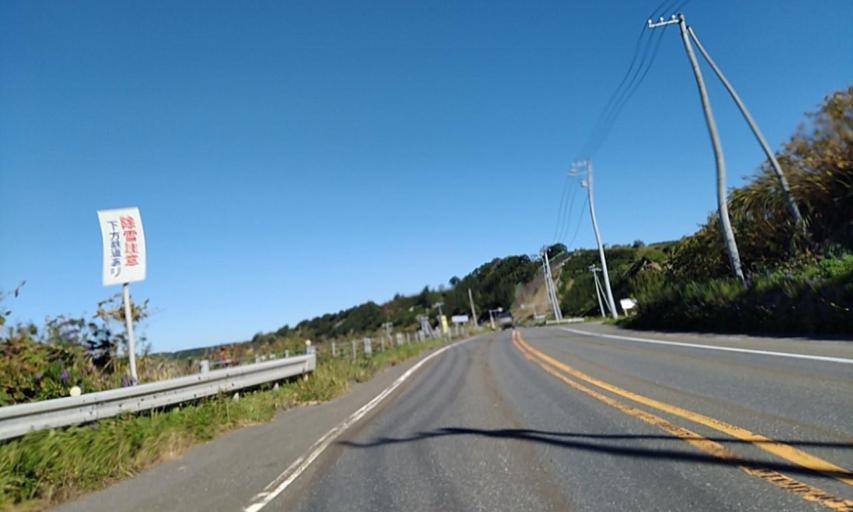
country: JP
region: Hokkaido
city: Shizunai-furukawacho
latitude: 42.4366
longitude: 142.2080
